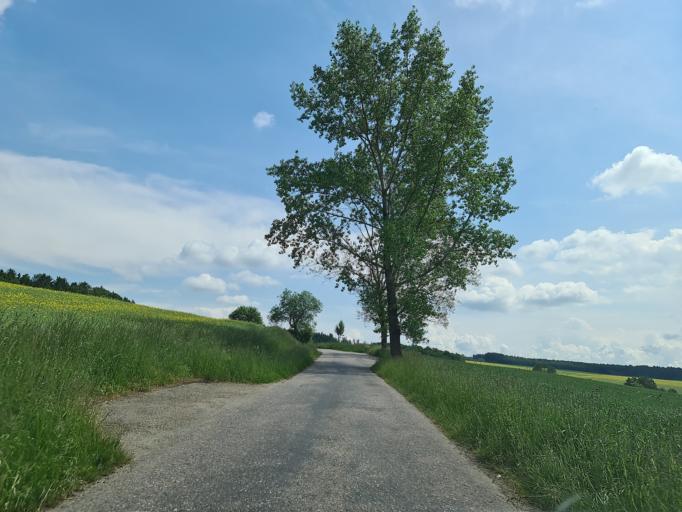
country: DE
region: Saxony
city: Stollberg
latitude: 50.6737
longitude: 12.7455
